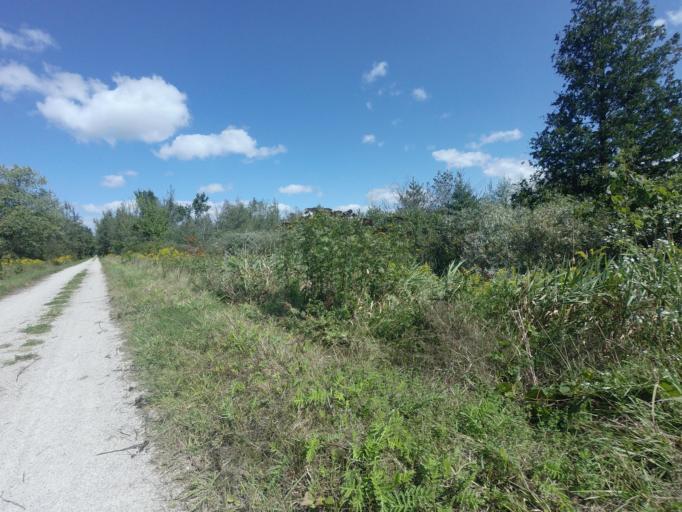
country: CA
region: Ontario
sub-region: Wellington County
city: Guelph
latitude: 43.7470
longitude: -80.3174
